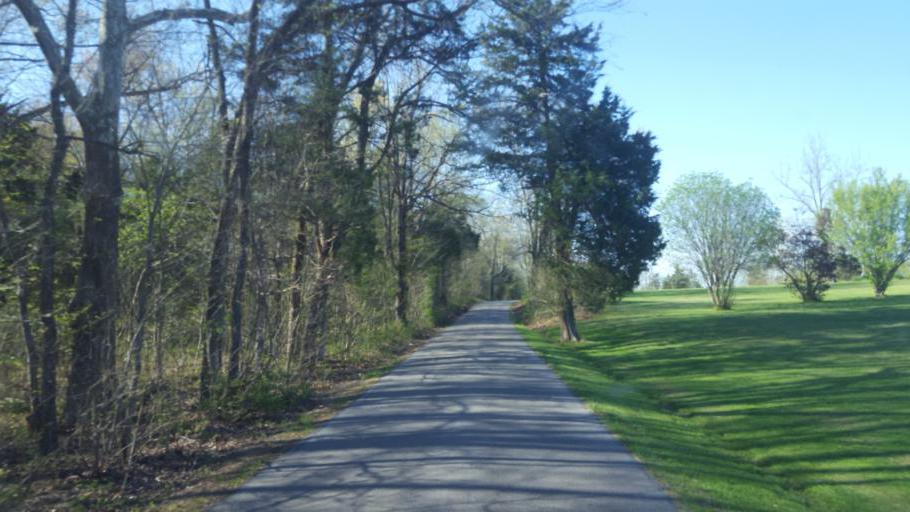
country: US
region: Kentucky
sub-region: Barren County
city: Cave City
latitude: 37.1701
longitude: -86.0426
